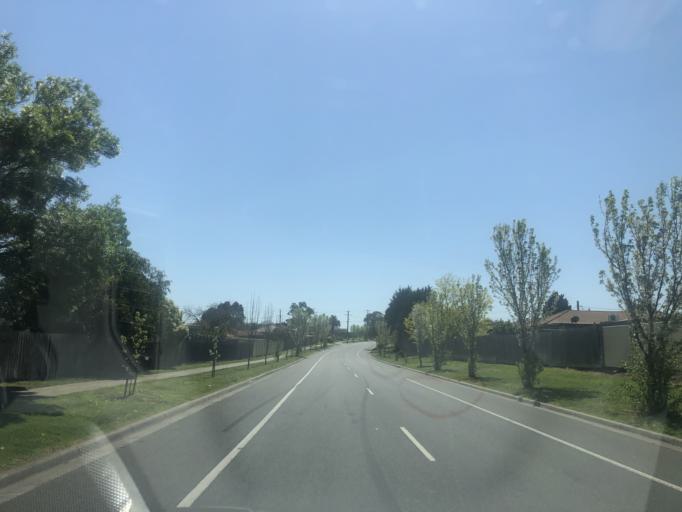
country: AU
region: Victoria
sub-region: Casey
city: Narre Warren South
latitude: -38.0436
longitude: 145.2790
